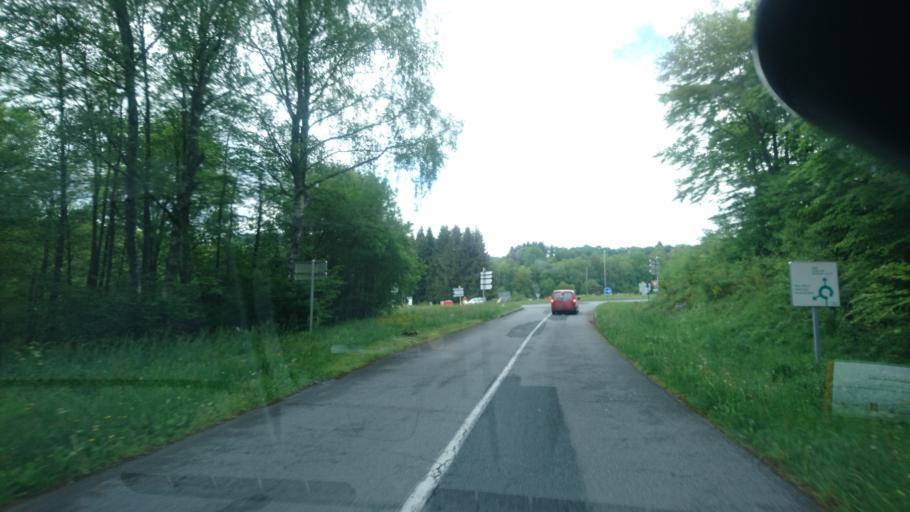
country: FR
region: Limousin
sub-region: Departement de la Haute-Vienne
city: Peyrat-le-Chateau
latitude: 45.8147
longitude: 1.9081
